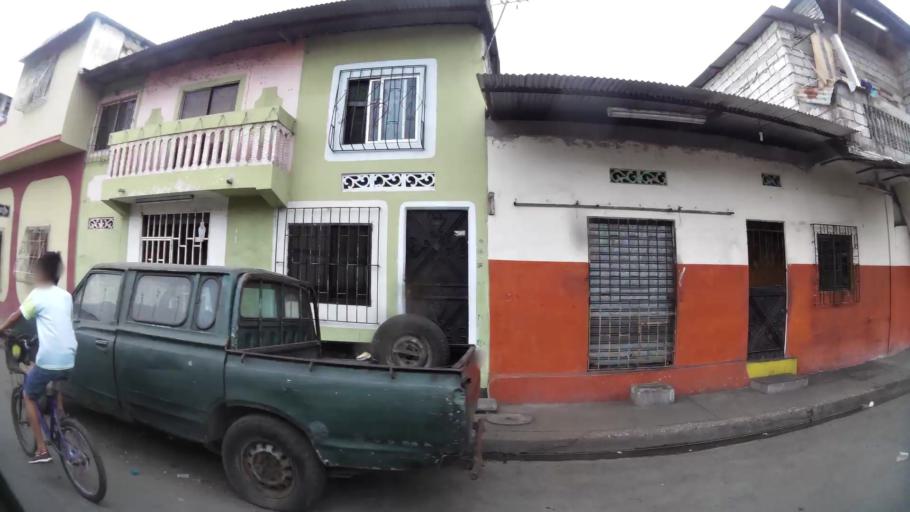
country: EC
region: Guayas
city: Guayaquil
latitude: -2.2294
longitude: -79.9095
